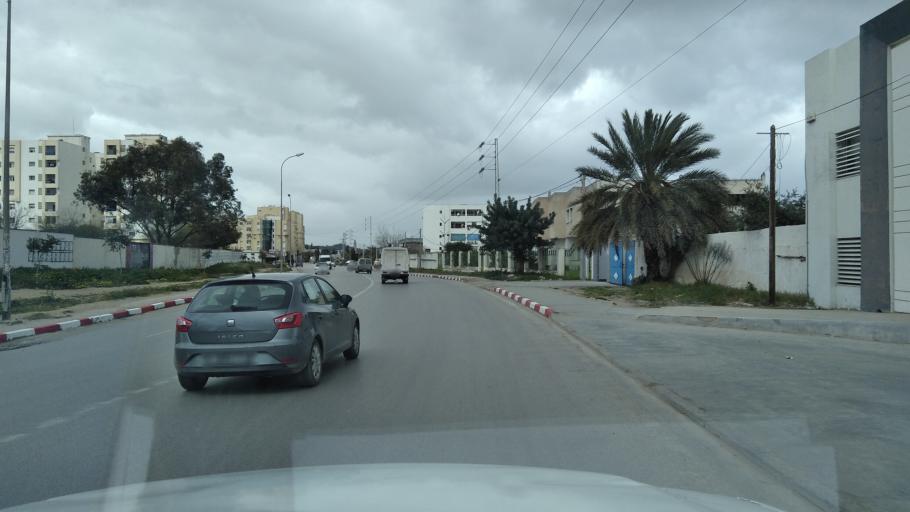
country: TN
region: Bin 'Arus
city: Ben Arous
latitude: 36.7458
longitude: 10.2331
